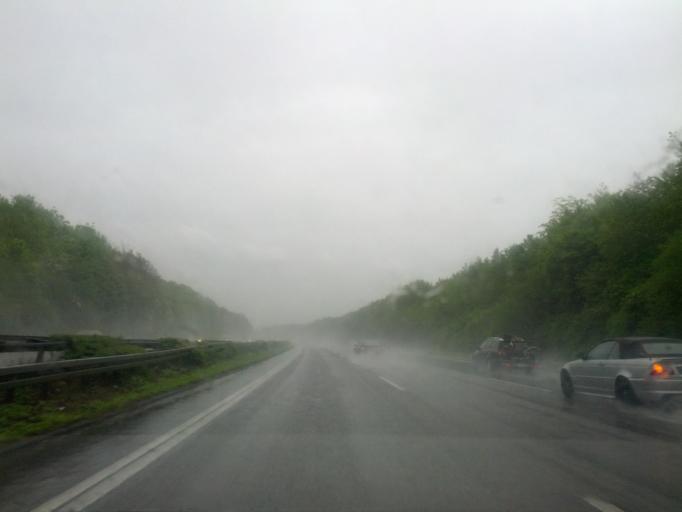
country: DE
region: North Rhine-Westphalia
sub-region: Regierungsbezirk Koln
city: Neustadt/Sued
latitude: 50.8876
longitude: 6.9343
